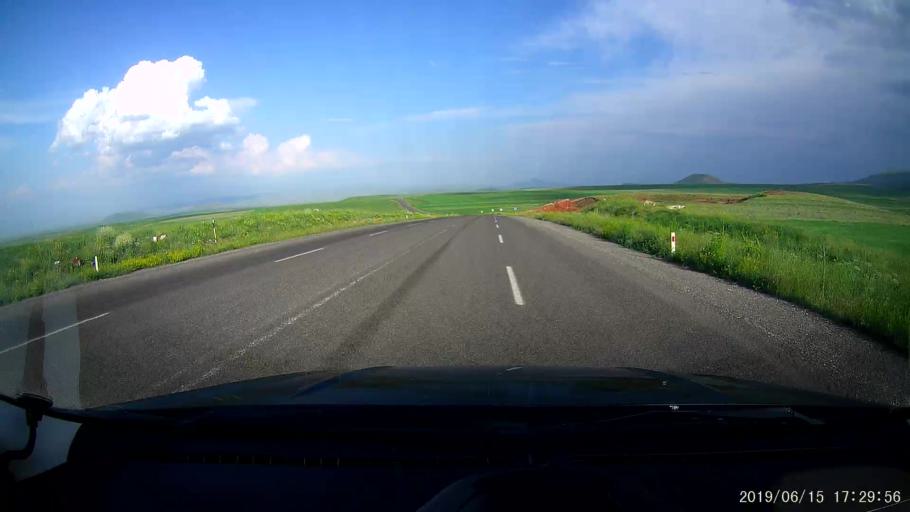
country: TR
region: Kars
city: Basgedikler
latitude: 40.5859
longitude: 43.4605
